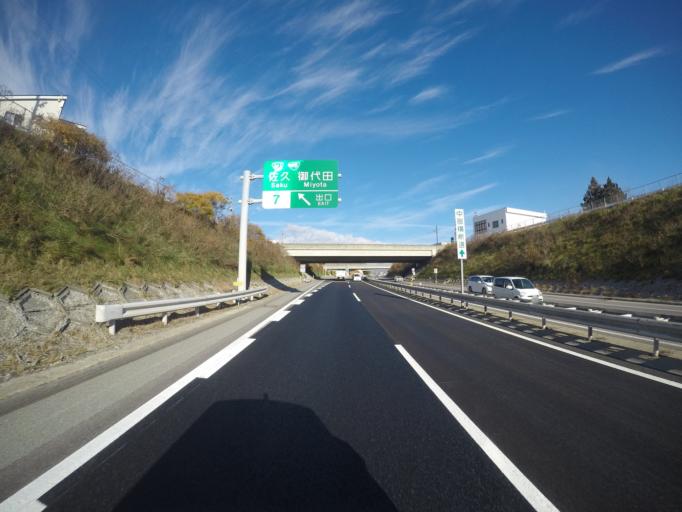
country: JP
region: Nagano
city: Komoro
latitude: 36.2846
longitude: 138.4853
